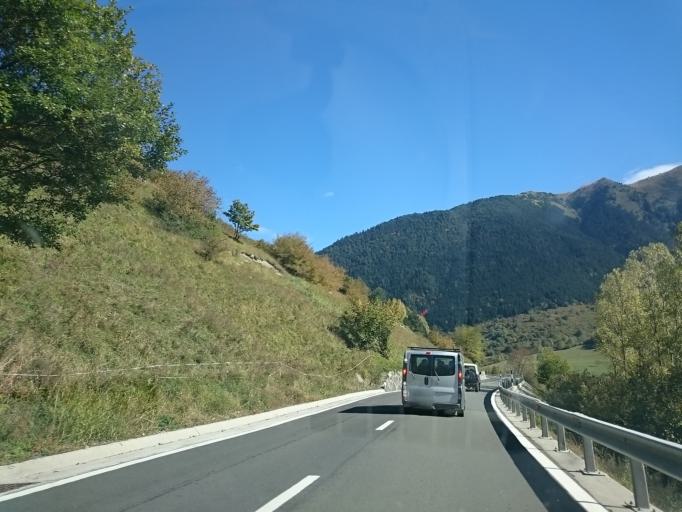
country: ES
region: Catalonia
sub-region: Provincia de Lleida
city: Vielha
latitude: 42.6766
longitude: 0.7765
